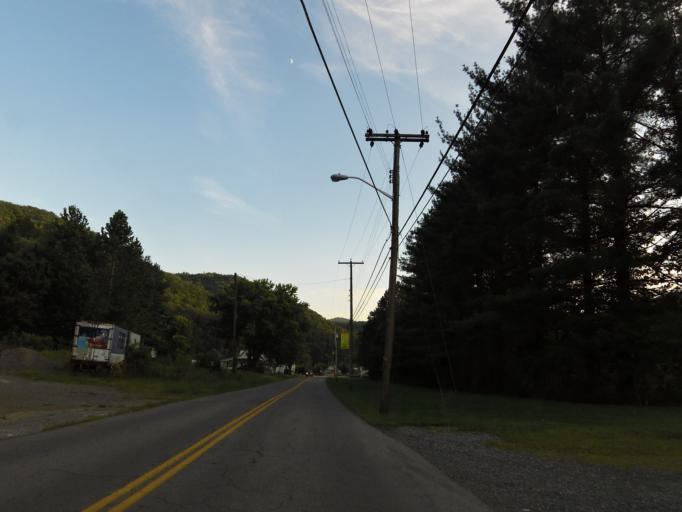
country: US
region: Virginia
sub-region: Washington County
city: Emory
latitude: 36.6284
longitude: -81.7895
